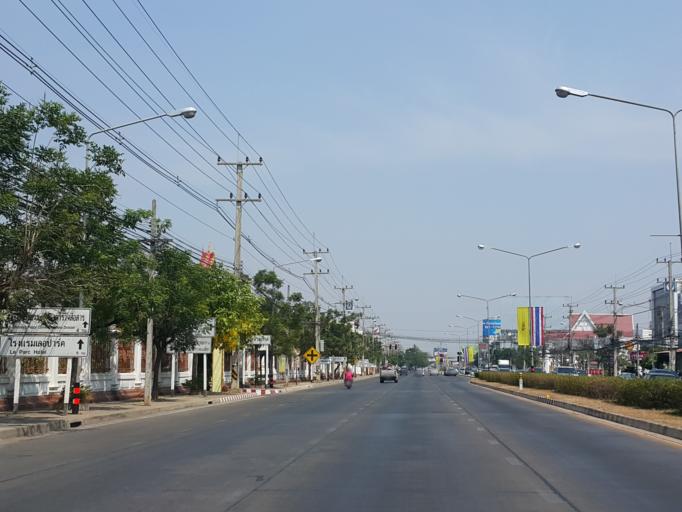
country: TH
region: Phitsanulok
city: Phitsanulok
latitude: 16.8276
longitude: 100.2540
